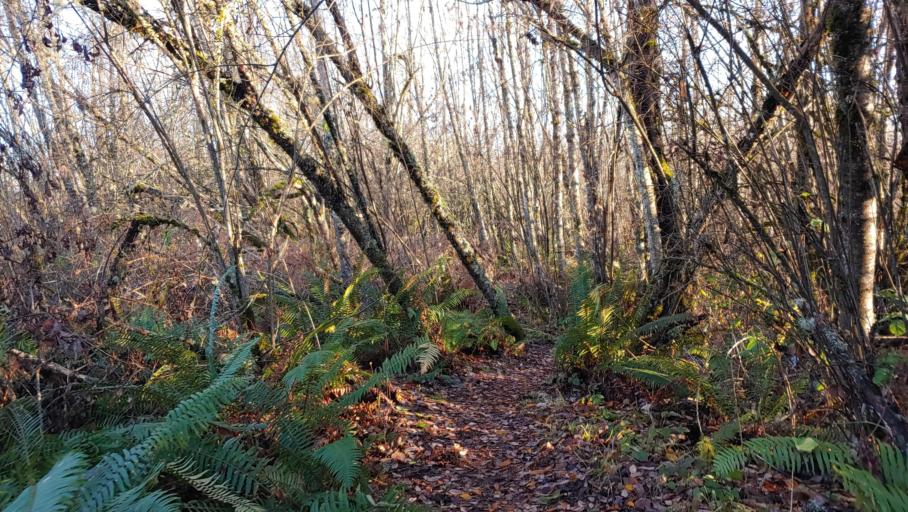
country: US
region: Washington
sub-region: King County
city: Renton
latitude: 47.4681
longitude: -122.1942
